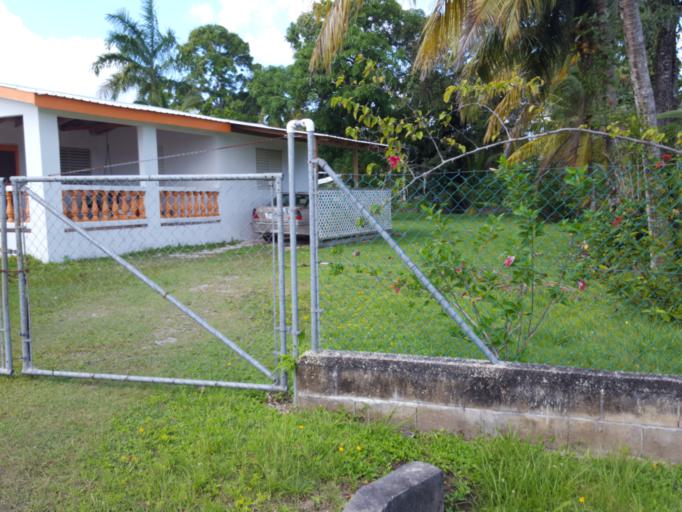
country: BZ
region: Belize
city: Belize City
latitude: 17.5675
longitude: -88.4060
